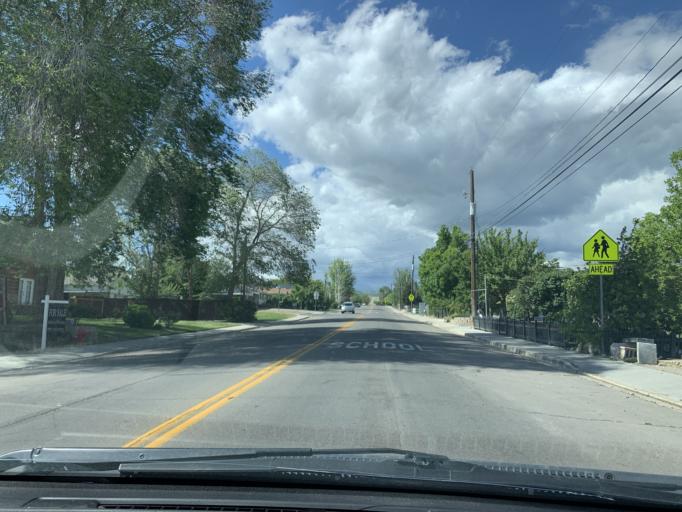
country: US
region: Utah
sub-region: Utah County
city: Lehi
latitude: 40.4005
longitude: -111.8398
